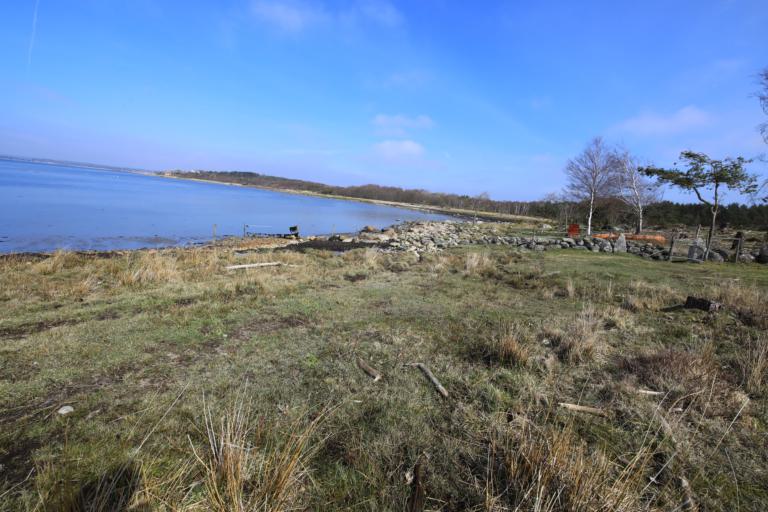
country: SE
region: Halland
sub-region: Kungsbacka Kommun
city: Frillesas
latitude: 57.2837
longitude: 12.1617
